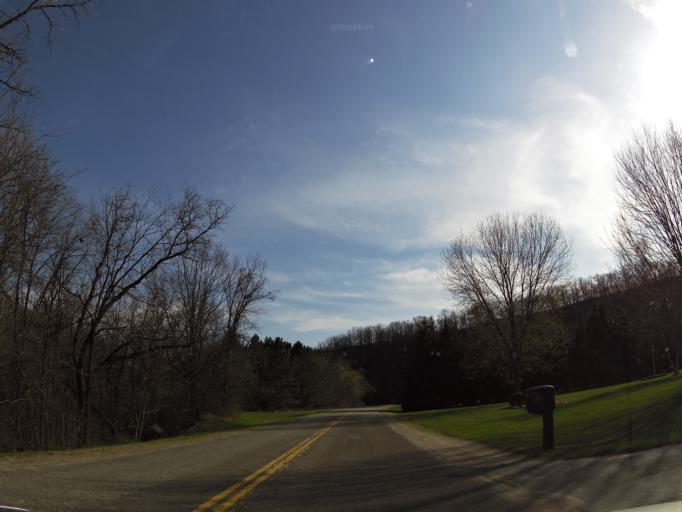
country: US
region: Wisconsin
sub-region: Pierce County
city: Ellsworth
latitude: 44.7033
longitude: -92.5763
